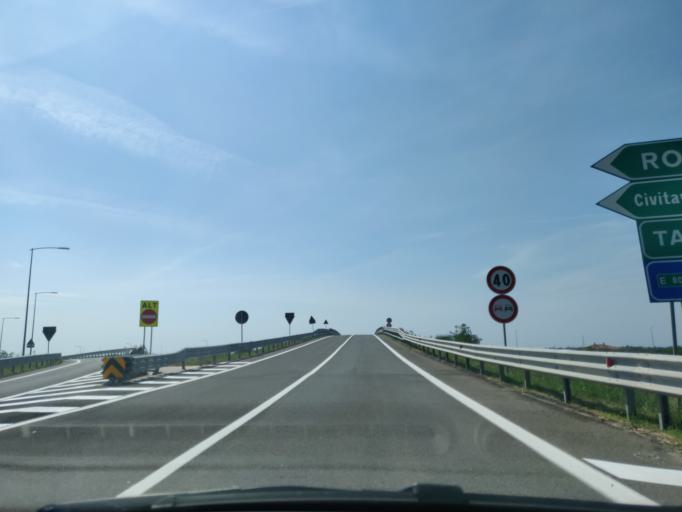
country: IT
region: Latium
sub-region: Provincia di Viterbo
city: Tarquinia
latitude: 42.2128
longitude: 11.7813
